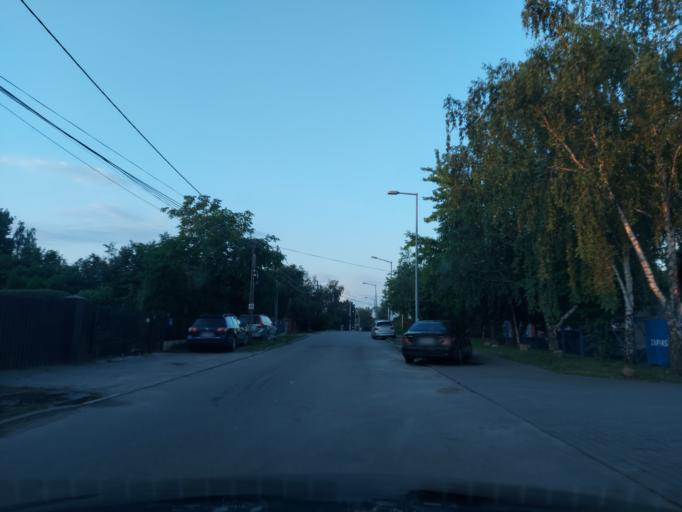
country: PL
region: Masovian Voivodeship
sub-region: Powiat piaseczynski
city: Piaseczno
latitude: 52.0828
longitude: 21.0173
